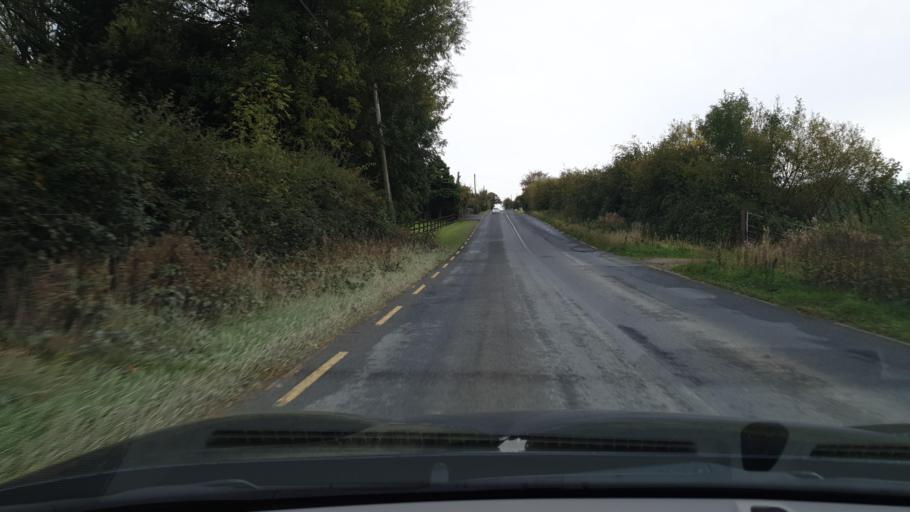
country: IE
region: Leinster
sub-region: Lu
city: Dunleer
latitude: 53.8092
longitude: -6.4354
